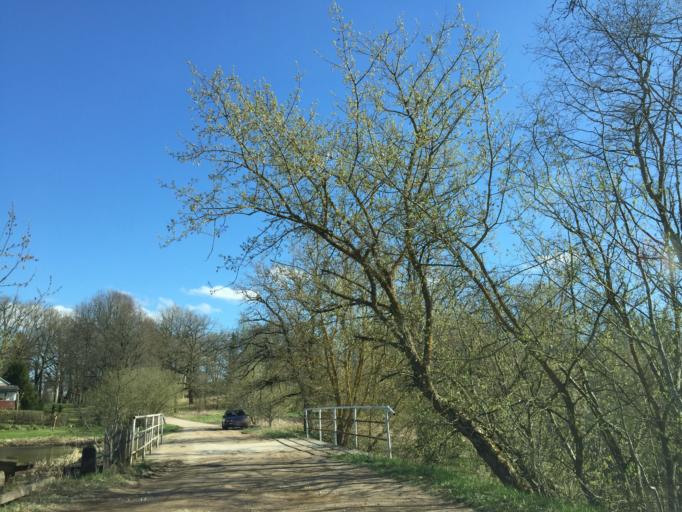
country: EE
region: Valgamaa
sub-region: Valga linn
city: Valga
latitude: 57.8692
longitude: 26.2448
